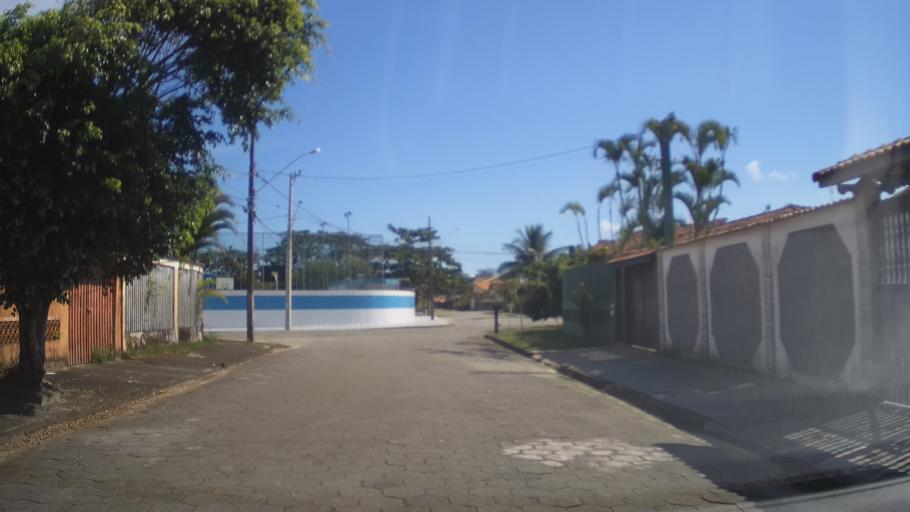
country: BR
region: Sao Paulo
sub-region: Itanhaem
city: Itanhaem
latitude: -24.1710
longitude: -46.7616
